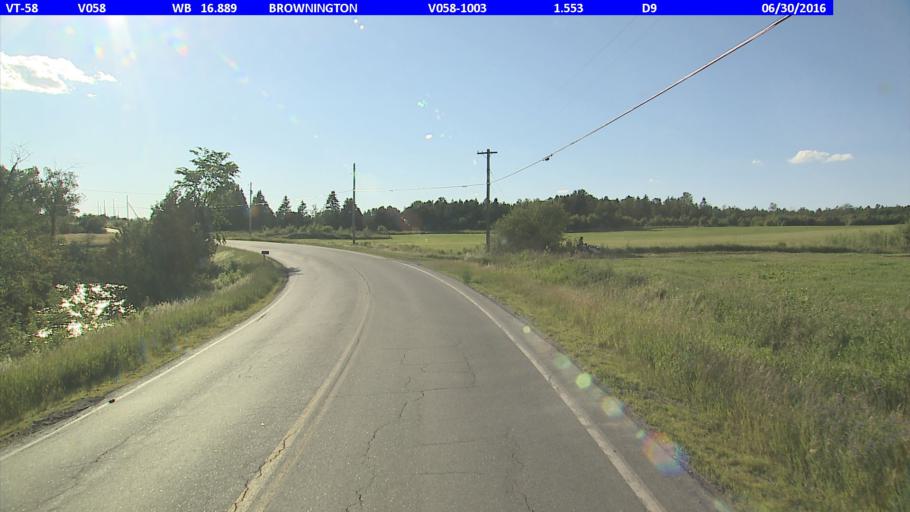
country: US
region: Vermont
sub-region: Orleans County
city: Newport
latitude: 44.7991
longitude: -72.1158
